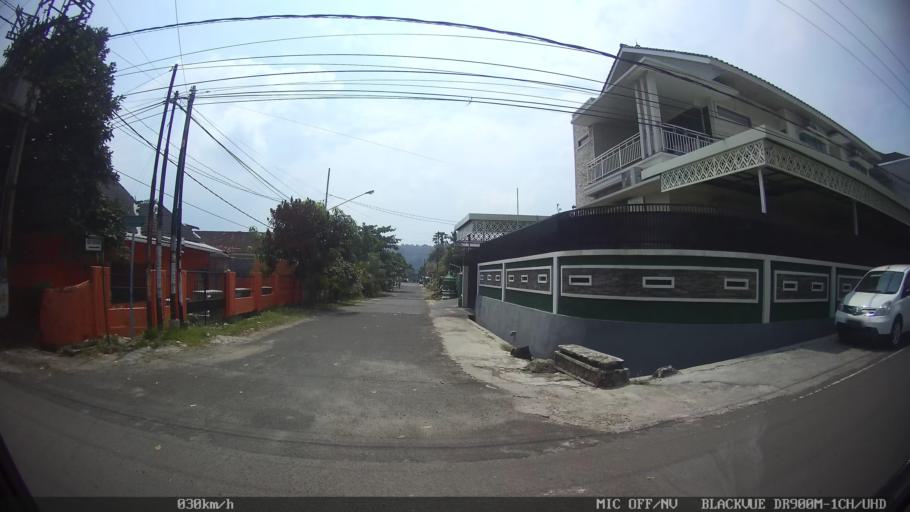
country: ID
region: Lampung
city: Bandarlampung
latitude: -5.4279
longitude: 105.2719
